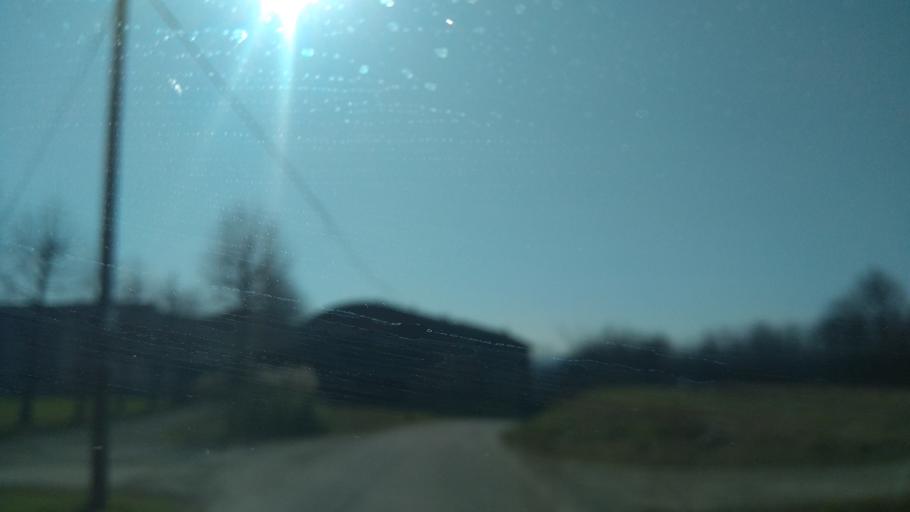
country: IT
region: Piedmont
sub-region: Provincia di Vercelli
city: Palazzolo Vercellese
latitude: 45.2170
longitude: 8.2304
